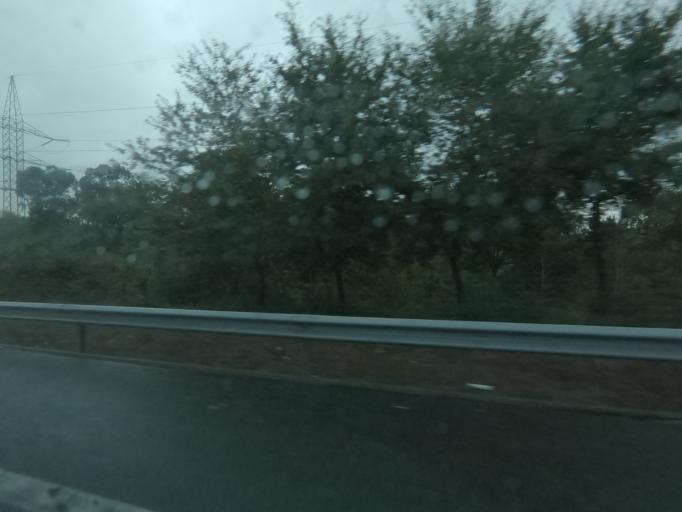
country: ES
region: Galicia
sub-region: Provincia de Pontevedra
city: Pontevedra
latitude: 42.3957
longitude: -8.6457
